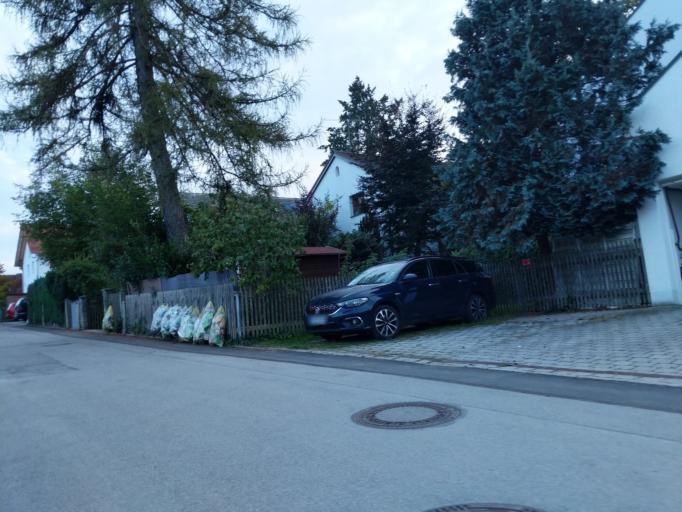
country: DE
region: Bavaria
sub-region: Upper Bavaria
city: Zorneding
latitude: 48.0883
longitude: 11.8339
